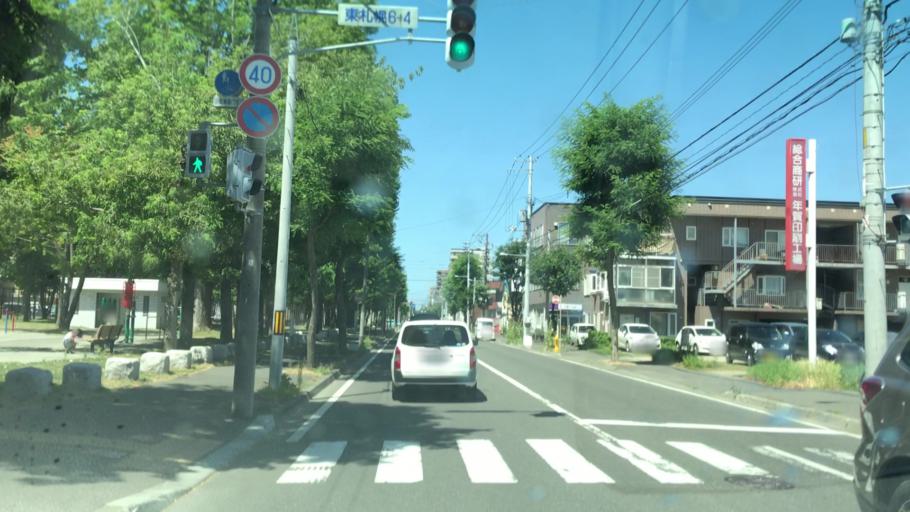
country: JP
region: Hokkaido
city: Sapporo
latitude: 43.0526
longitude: 141.3955
